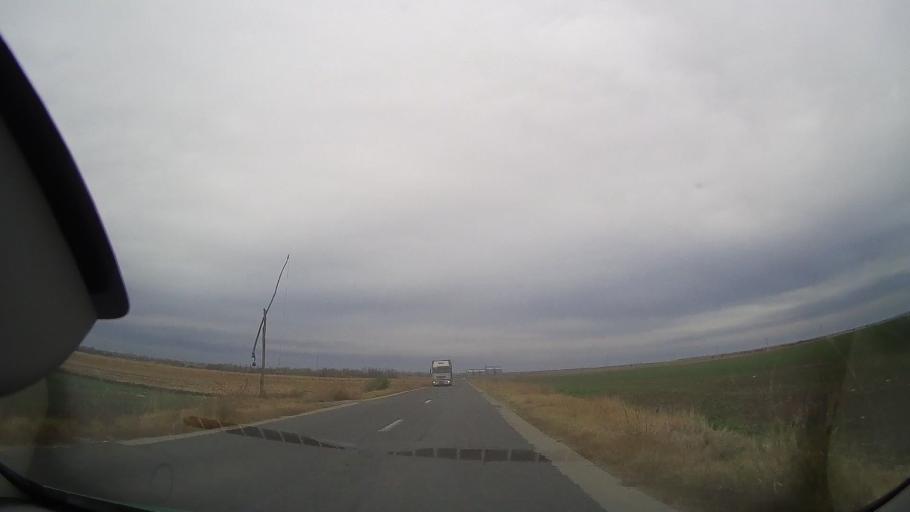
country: RO
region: Ialomita
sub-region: Comuna Milosesti
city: Milosesti
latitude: 44.7606
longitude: 27.1979
